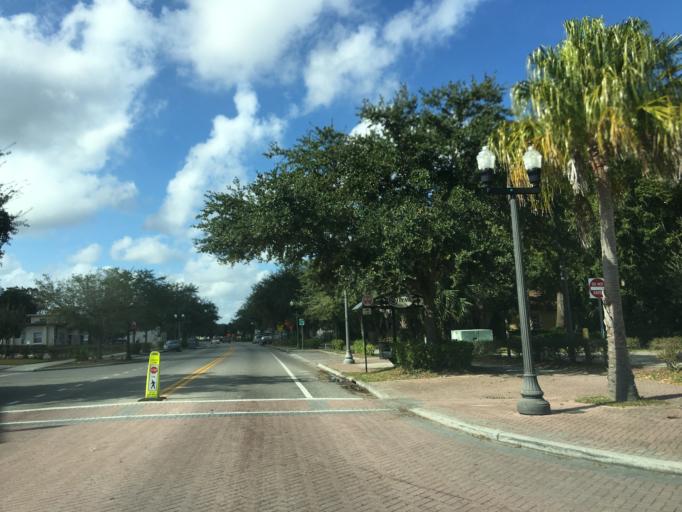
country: US
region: Florida
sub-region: Orange County
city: Eatonville
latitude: 28.6185
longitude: -81.3793
